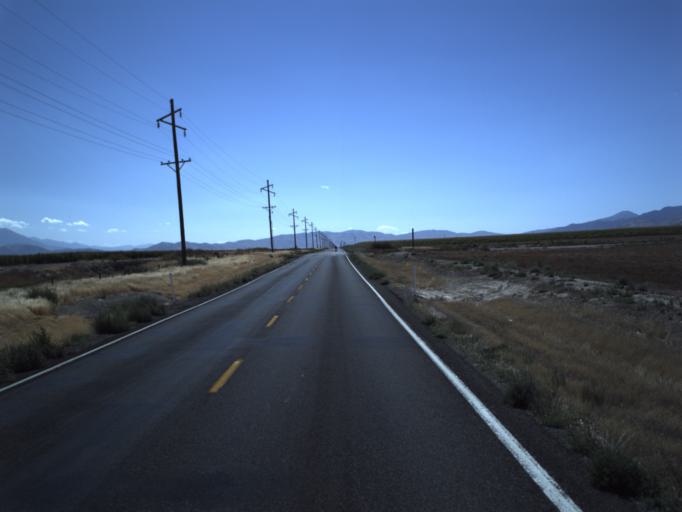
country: US
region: Utah
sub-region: Utah County
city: Genola
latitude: 40.0993
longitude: -111.9591
